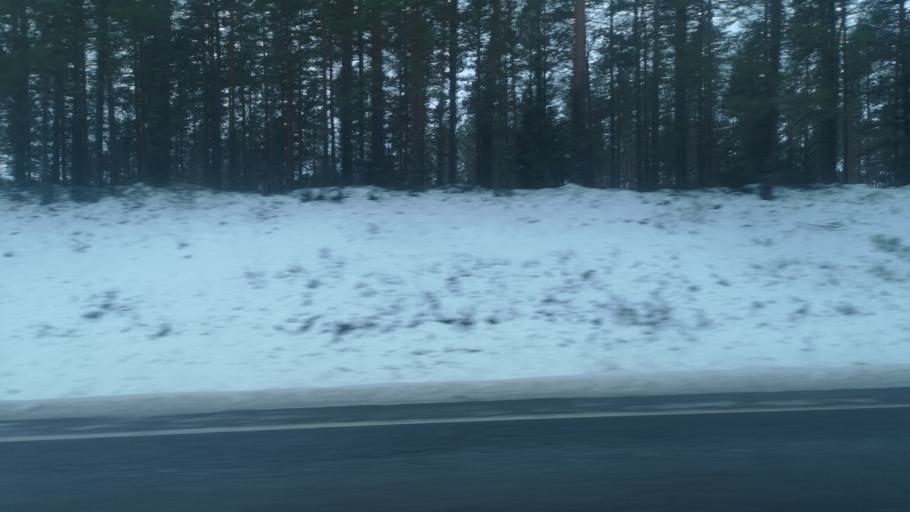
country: FI
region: Varsinais-Suomi
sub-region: Salo
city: Muurla
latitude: 60.3072
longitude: 23.3176
